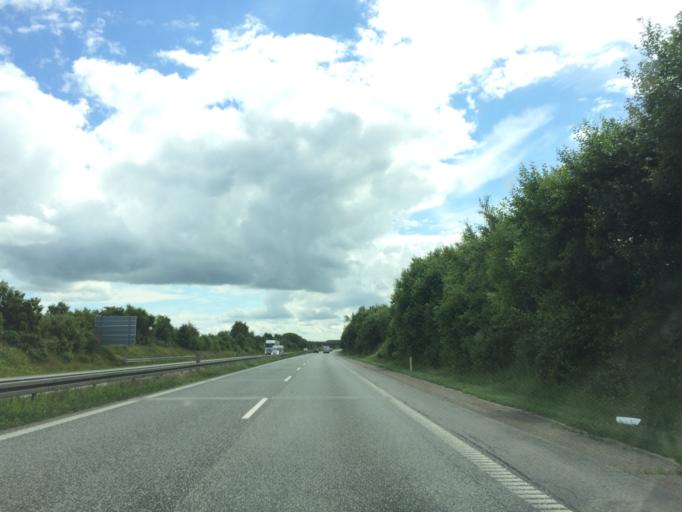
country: DK
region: North Denmark
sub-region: Mariagerfjord Kommune
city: Hobro
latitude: 56.6587
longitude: 9.7360
